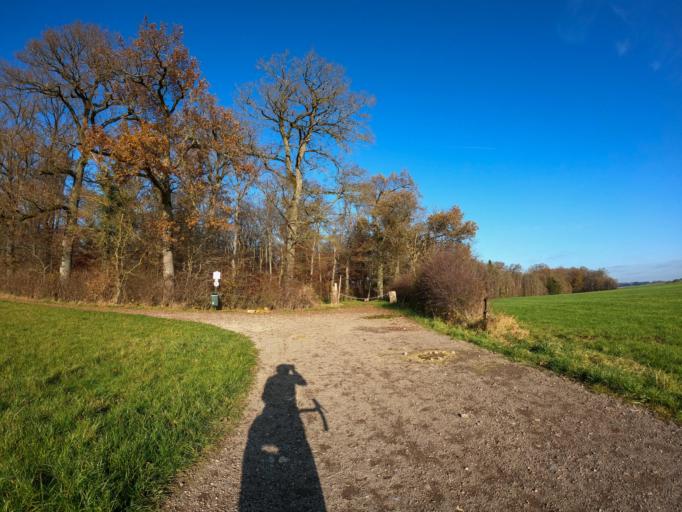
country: LU
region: Luxembourg
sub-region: Canton de Capellen
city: Kehlen
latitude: 49.6797
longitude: 6.0219
